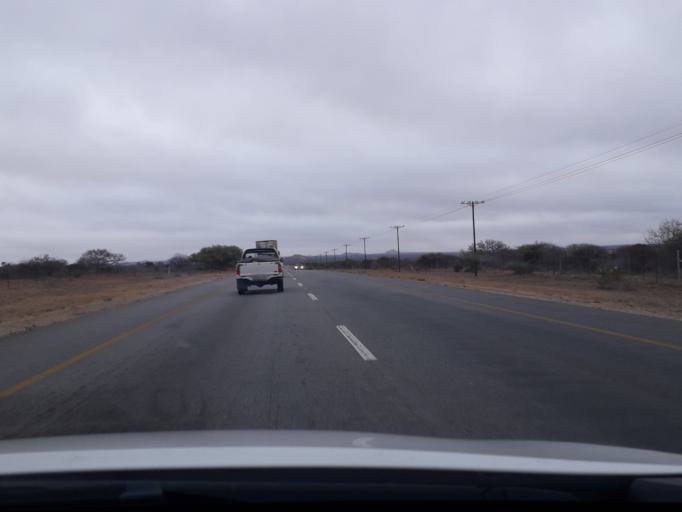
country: ZA
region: Limpopo
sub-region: Capricorn District Municipality
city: Mankoeng
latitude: -23.5654
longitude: 29.6798
